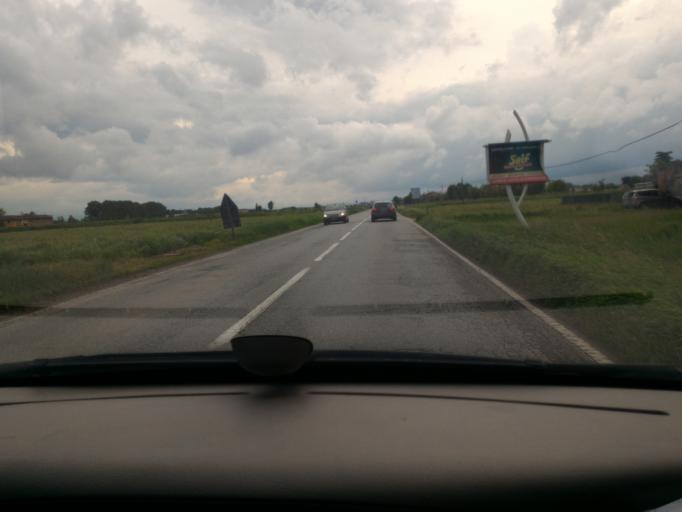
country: IT
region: Piedmont
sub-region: Provincia di Cuneo
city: Savigliano
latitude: 44.6250
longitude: 7.6656
